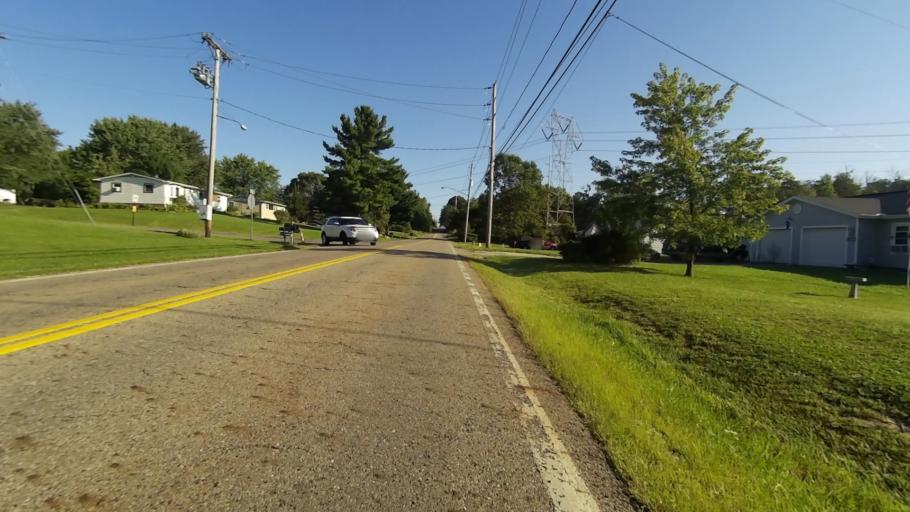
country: US
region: Ohio
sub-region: Portage County
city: Streetsboro
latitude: 41.2466
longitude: -81.3266
